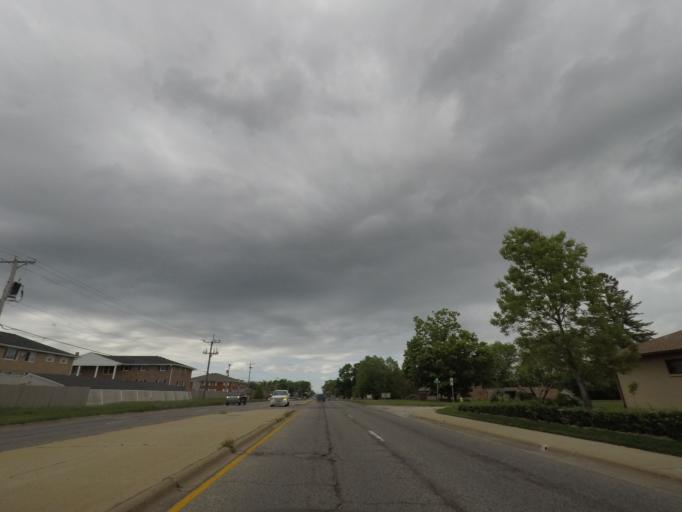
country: US
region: Illinois
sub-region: Winnebago County
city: Rockford
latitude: 42.2419
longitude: -89.0290
